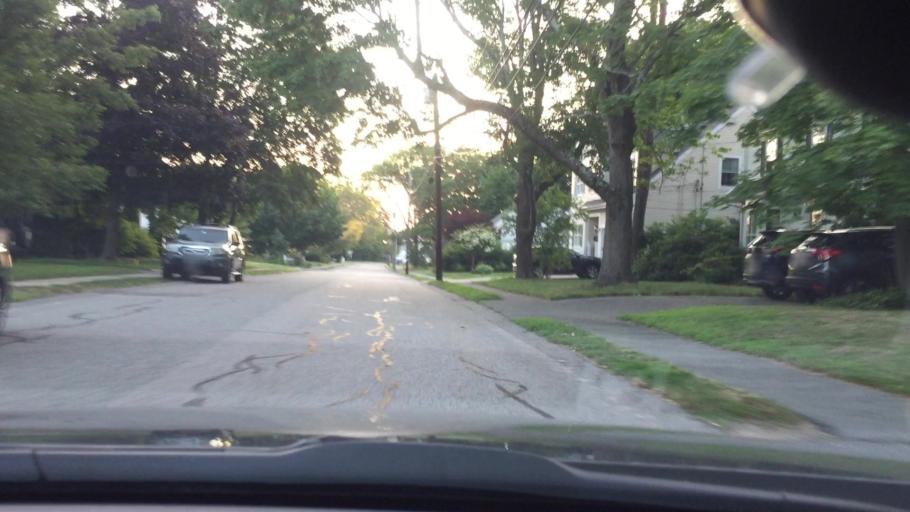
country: US
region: Massachusetts
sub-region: Norfolk County
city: Needham
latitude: 42.2911
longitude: -71.2322
